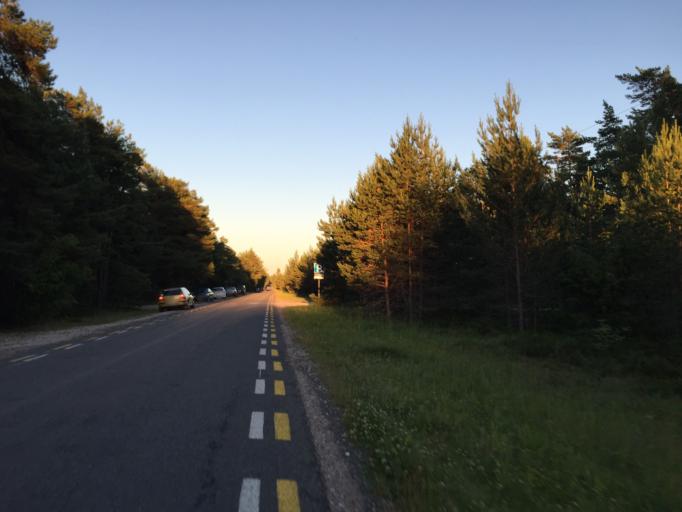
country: EE
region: Harju
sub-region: Raasiku vald
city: Raasiku
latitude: 59.5099
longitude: 25.2732
